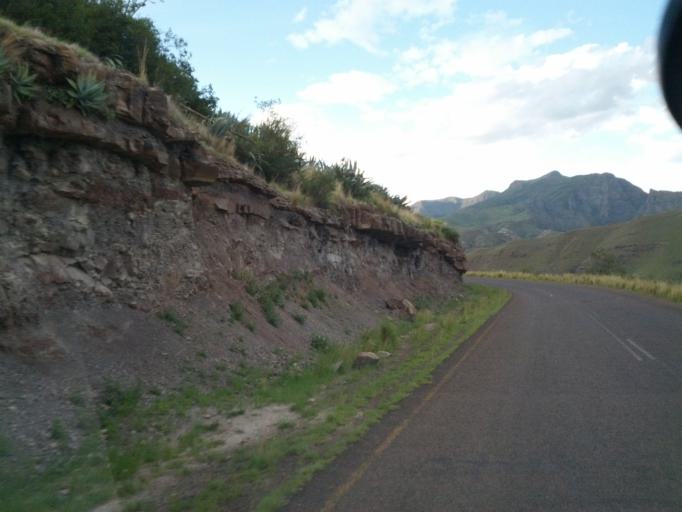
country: LS
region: Qacha's Nek
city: Qacha's Nek
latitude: -30.0727
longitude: 28.5603
